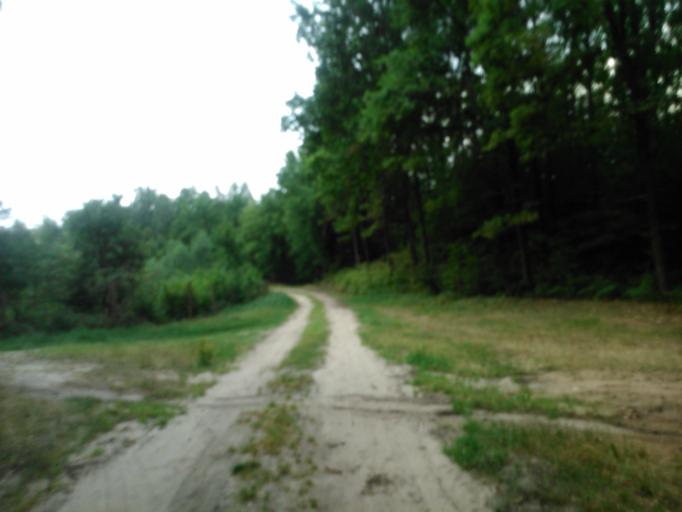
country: PL
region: Kujawsko-Pomorskie
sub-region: Powiat brodnicki
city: Gorzno
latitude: 53.2109
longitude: 19.7124
